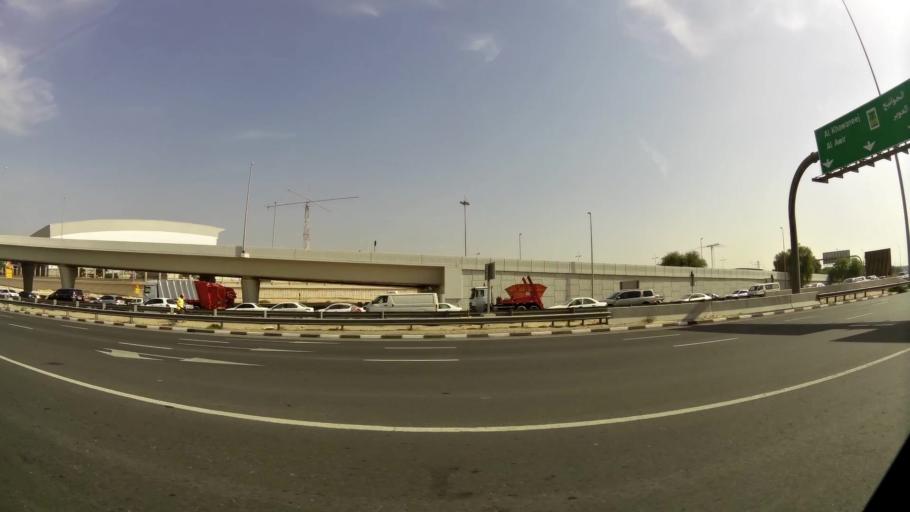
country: AE
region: Ash Shariqah
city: Sharjah
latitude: 25.2302
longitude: 55.3973
